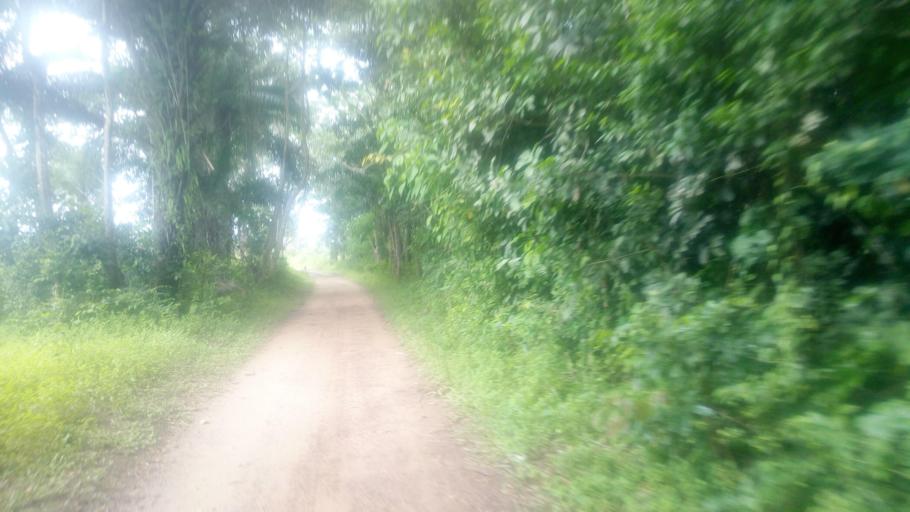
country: SL
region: Northern Province
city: Magburaka
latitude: 8.6795
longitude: -12.0683
